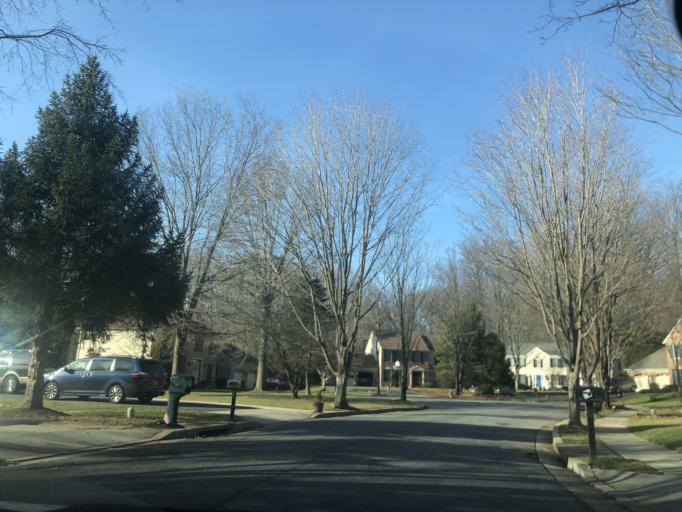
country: US
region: Maryland
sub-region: Howard County
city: Columbia
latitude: 39.2905
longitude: -76.8447
